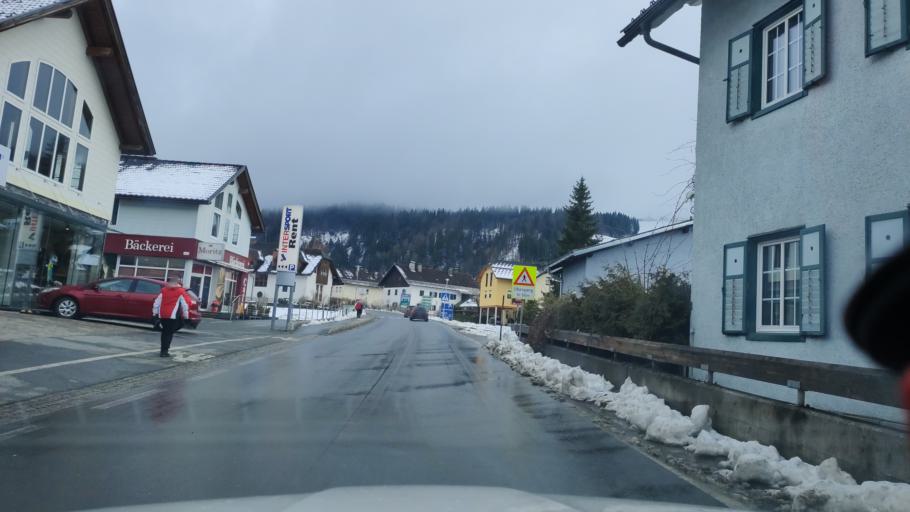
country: AT
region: Carinthia
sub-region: Politischer Bezirk Hermagor
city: Hermagor
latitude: 46.6149
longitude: 13.2804
